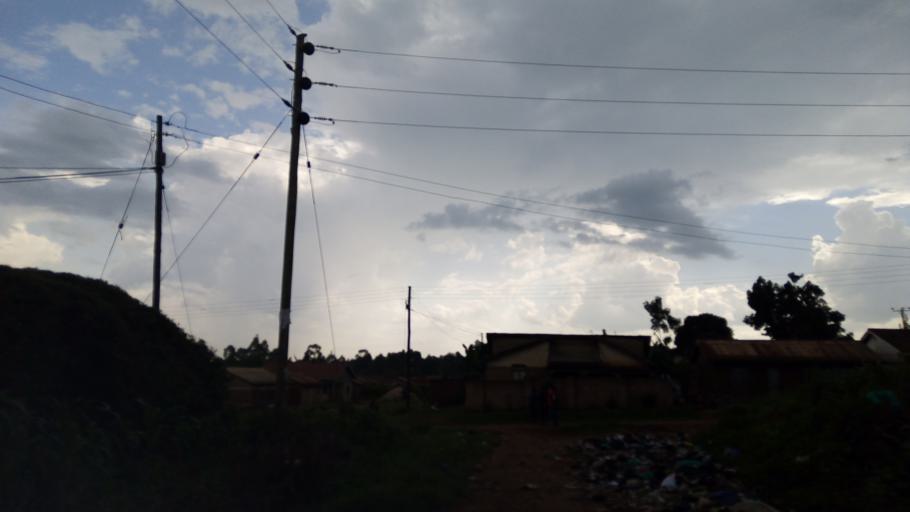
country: UG
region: Eastern Region
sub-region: Mbale District
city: Mbale
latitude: 1.0668
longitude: 34.1643
